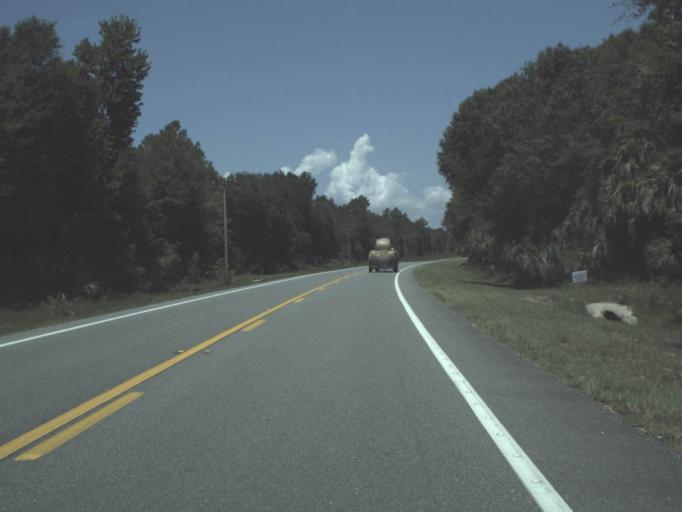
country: US
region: Florida
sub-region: Taylor County
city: Perry
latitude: 30.1413
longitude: -83.9310
